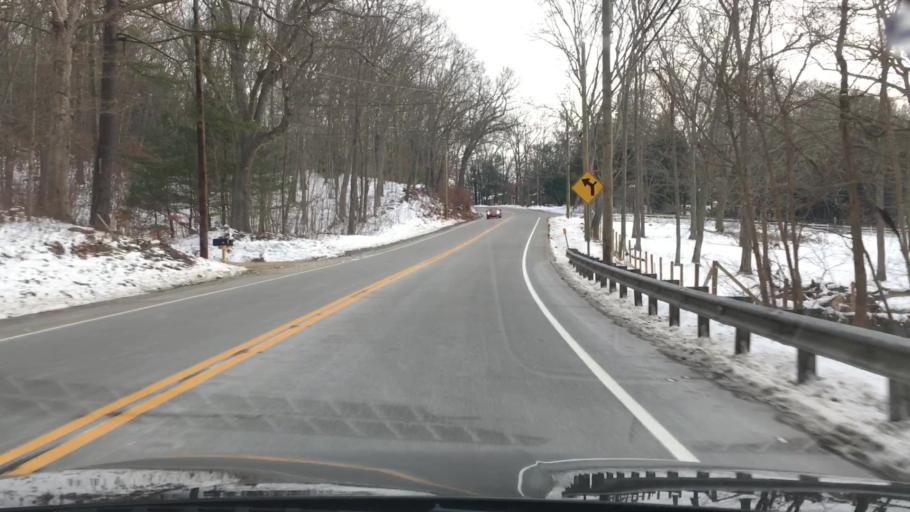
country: US
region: Connecticut
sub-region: Tolland County
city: Storrs
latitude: 41.8533
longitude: -72.1864
